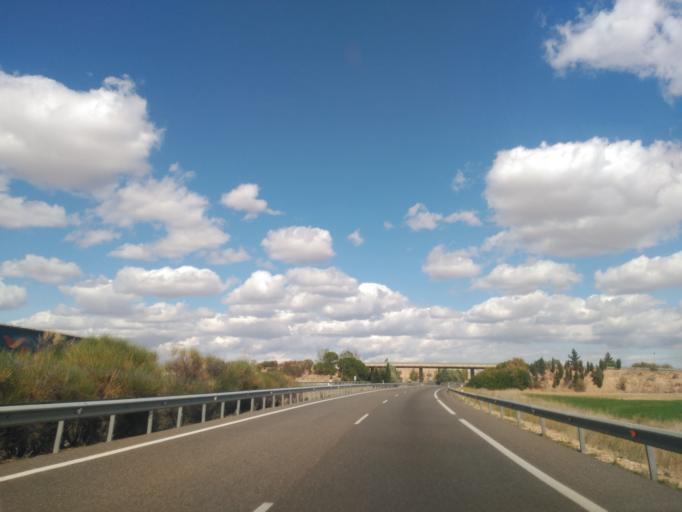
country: ES
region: Castille and Leon
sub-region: Provincia de Palencia
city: Soto de Cerrato
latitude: 41.9854
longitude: -4.4303
